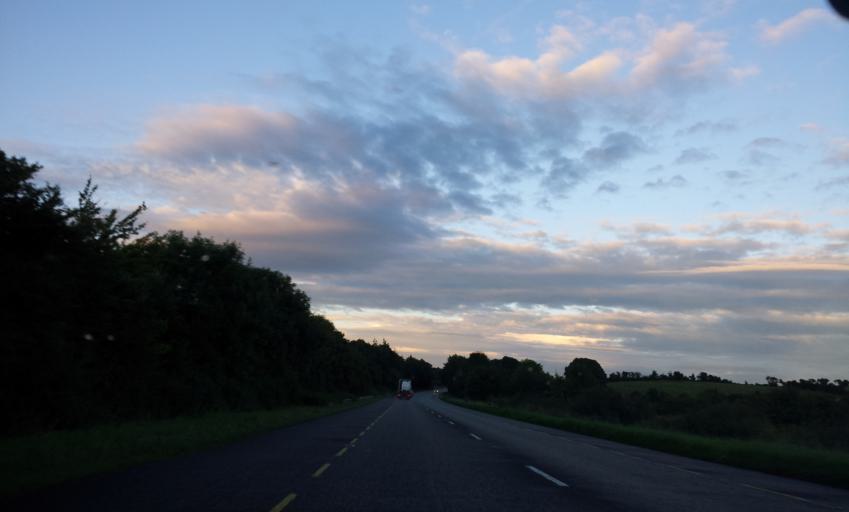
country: IE
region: Munster
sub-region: County Limerick
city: Rathkeale
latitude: 52.5303
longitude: -8.9282
